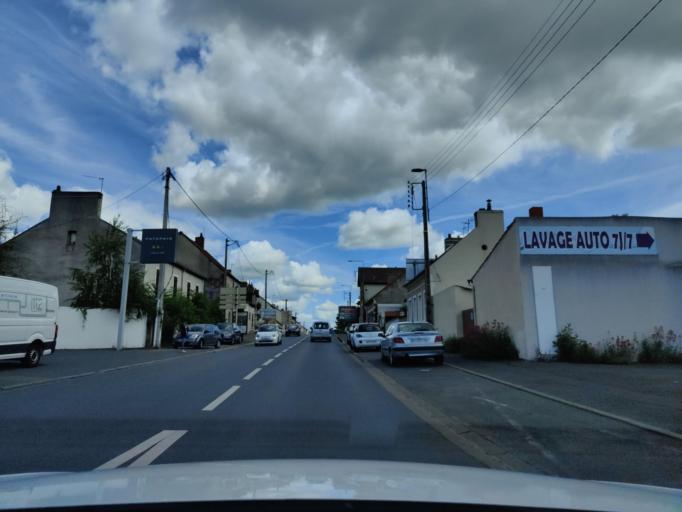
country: FR
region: Auvergne
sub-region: Departement de l'Allier
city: Desertines
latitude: 46.3466
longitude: 2.6095
